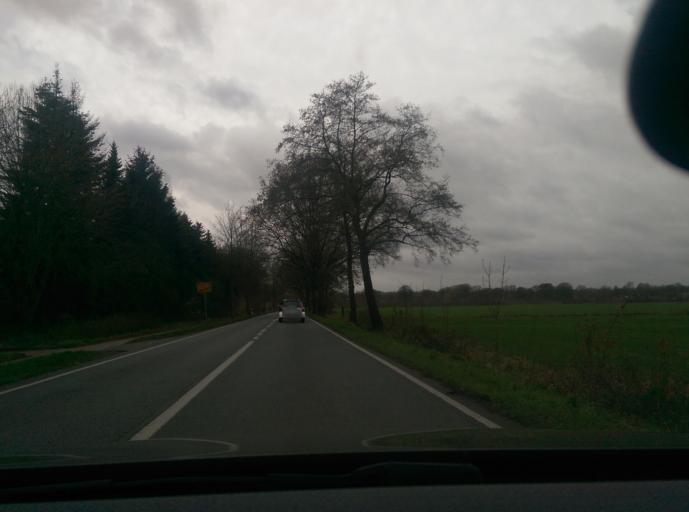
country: DE
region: Lower Saxony
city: Elze
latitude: 52.5508
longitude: 9.7624
